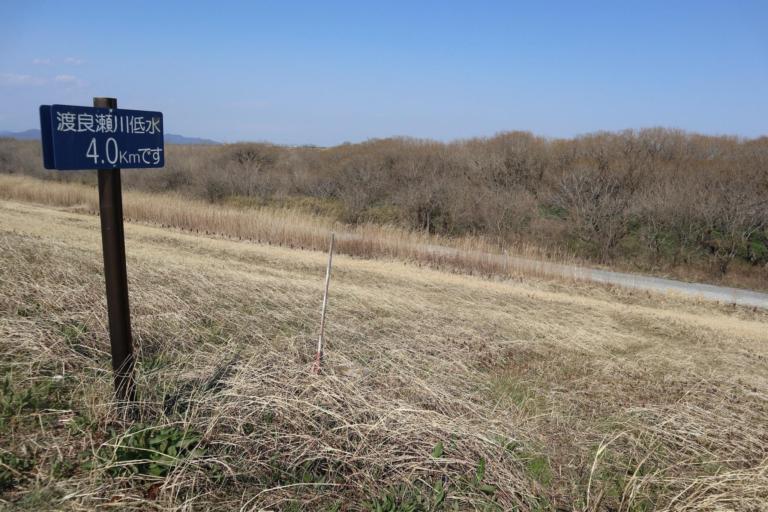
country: JP
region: Tochigi
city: Fujioka
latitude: 36.2297
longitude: 139.6865
